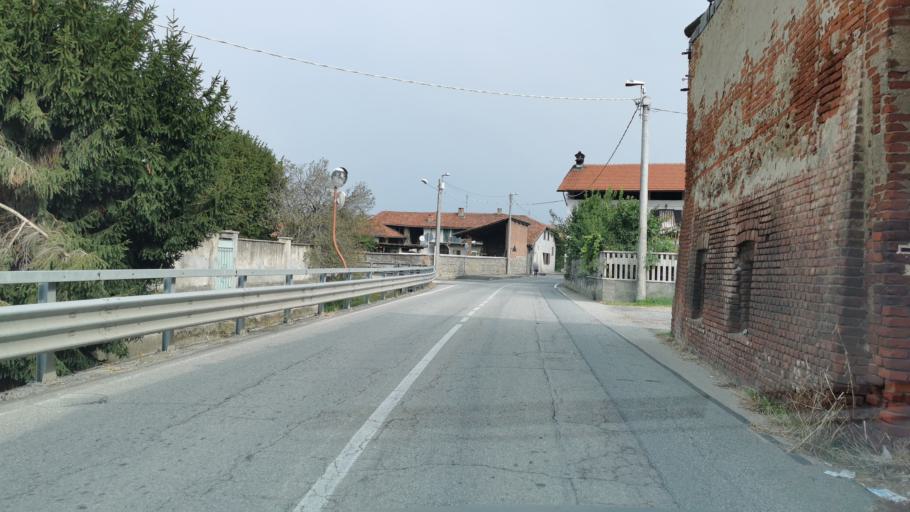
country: IT
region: Piedmont
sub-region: Provincia di Torino
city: San Benigno Canavese
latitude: 45.2259
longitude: 7.7865
